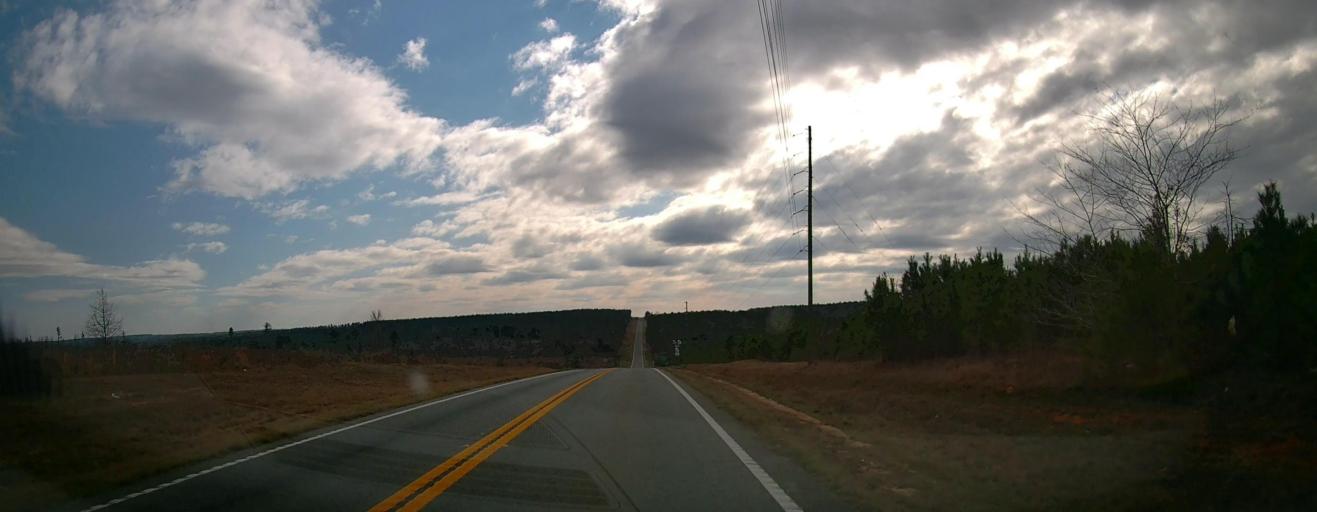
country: US
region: Georgia
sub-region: Taylor County
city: Butler
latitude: 32.4483
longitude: -84.3647
